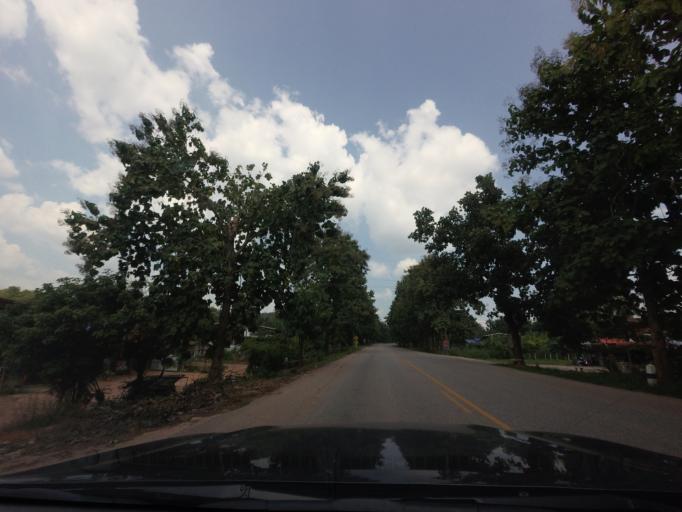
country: TH
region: Phitsanulok
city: Chat Trakan
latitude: 17.2817
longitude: 100.5322
